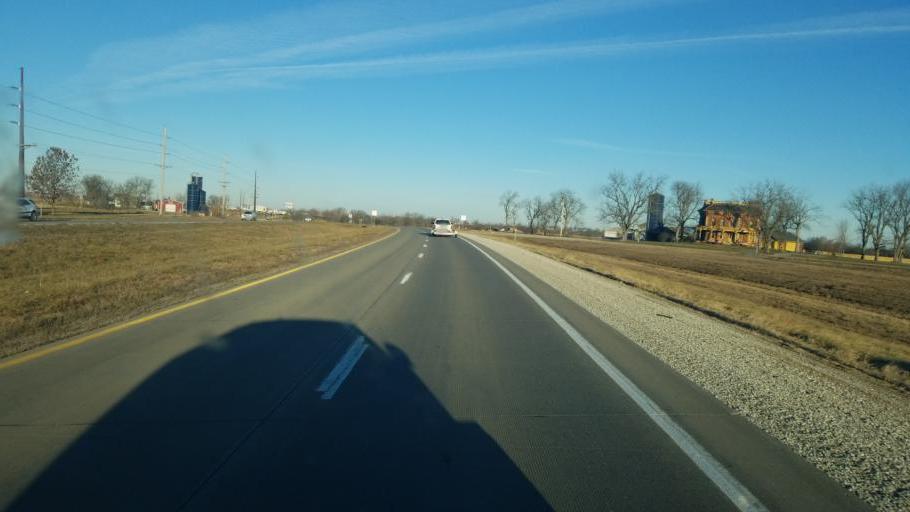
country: US
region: Iowa
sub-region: Marion County
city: Pella
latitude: 41.3834
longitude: -92.8220
